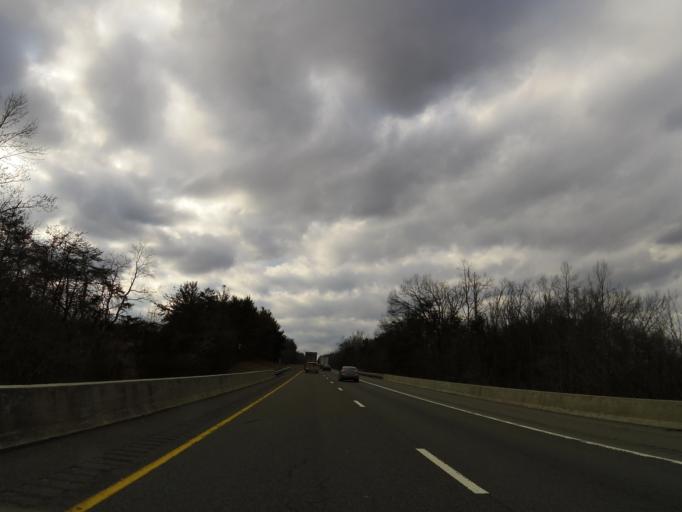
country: US
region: Tennessee
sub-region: Cumberland County
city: Crossville
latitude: 36.0163
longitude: -85.0697
